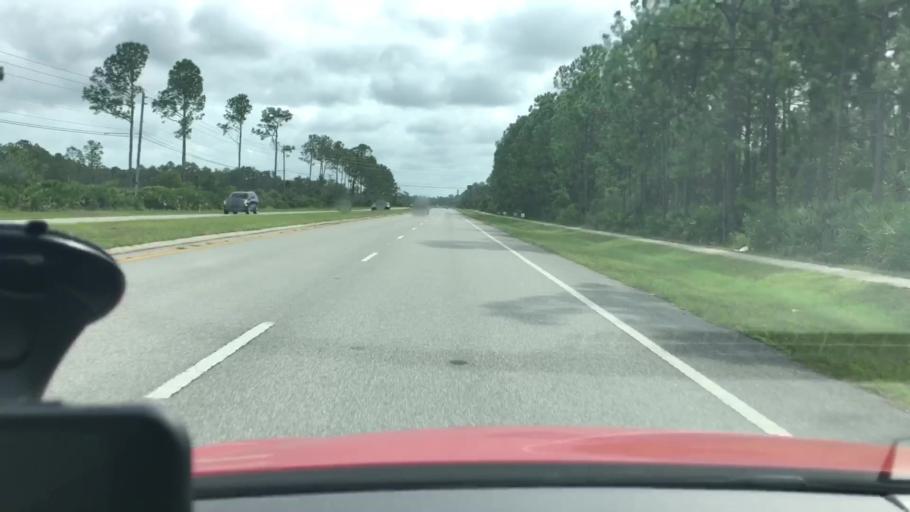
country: US
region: Florida
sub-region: Volusia County
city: Ormond Beach
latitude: 29.2581
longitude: -81.0938
